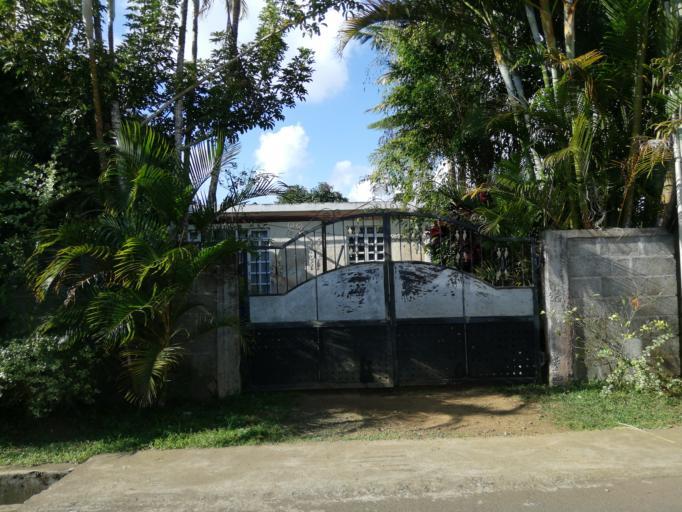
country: MU
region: Moka
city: Verdun
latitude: -20.2186
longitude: 57.5430
